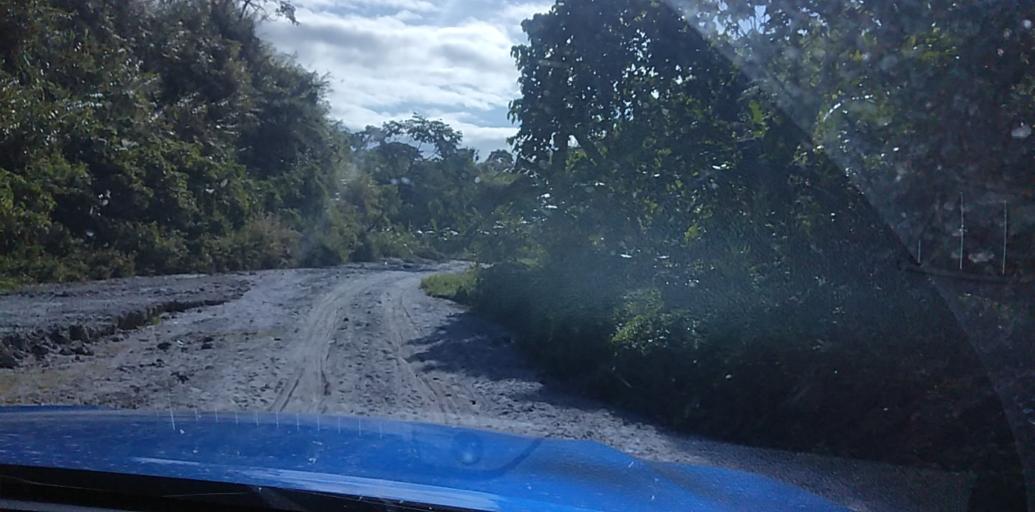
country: PH
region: Central Luzon
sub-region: Province of Pampanga
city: Babo-Pangulo
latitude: 15.1496
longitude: 120.4367
